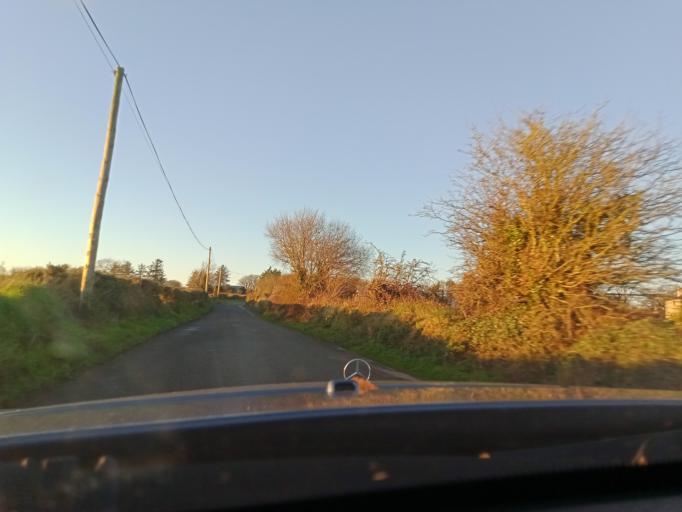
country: IE
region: Munster
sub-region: Waterford
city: Waterford
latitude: 52.3717
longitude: -7.1271
